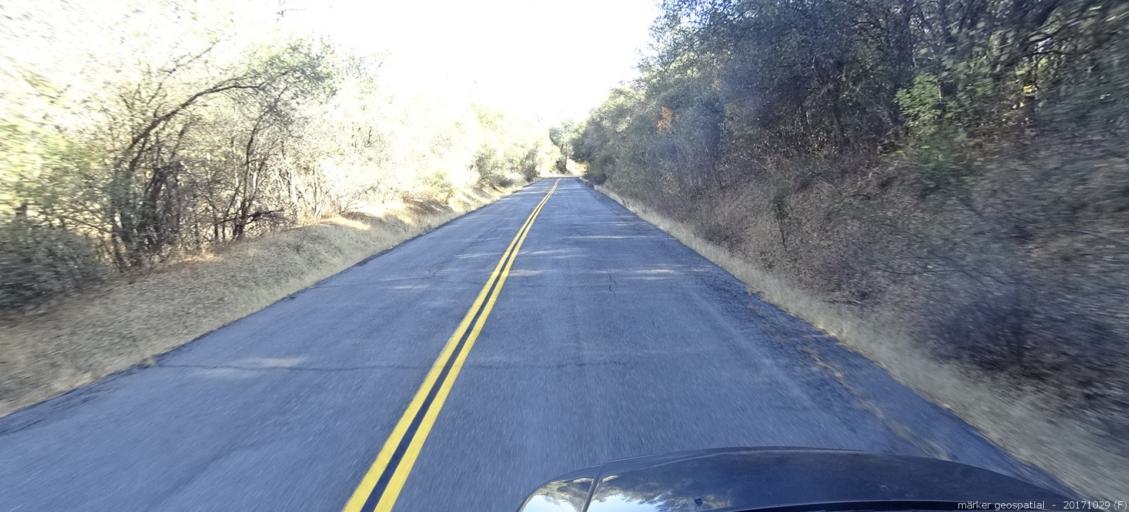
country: US
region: California
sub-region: Trinity County
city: Lewiston
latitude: 40.3977
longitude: -122.7860
